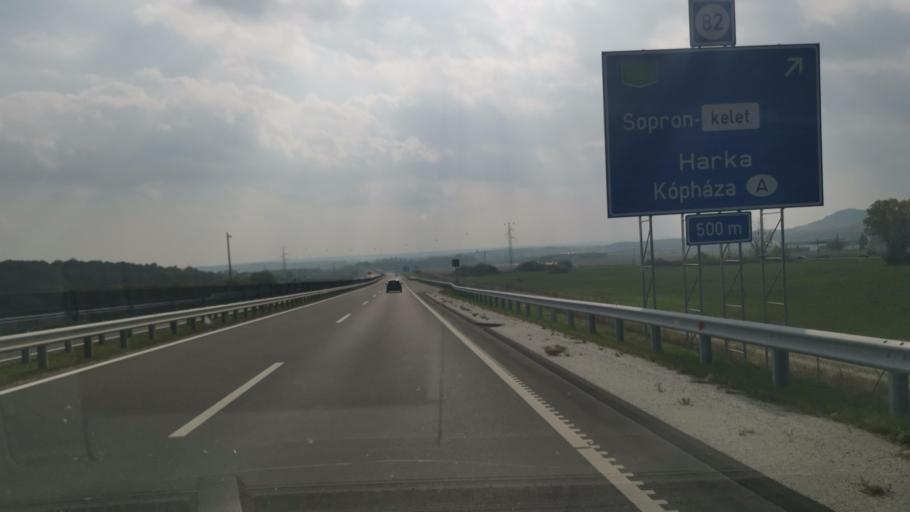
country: HU
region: Gyor-Moson-Sopron
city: Sopron
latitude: 47.6640
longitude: 16.6276
